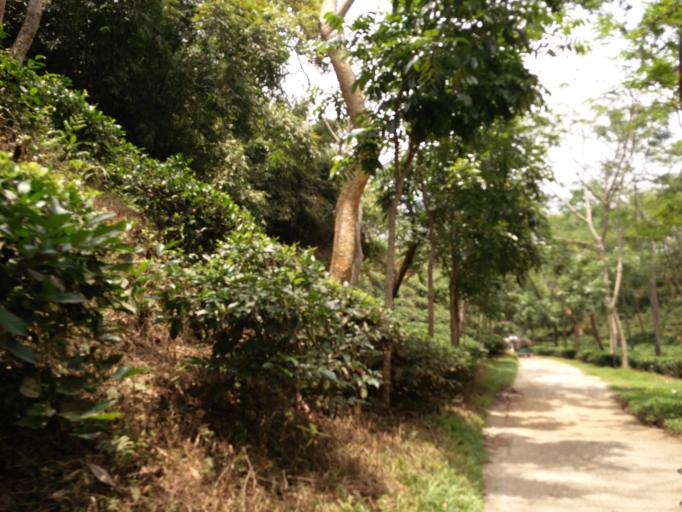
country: IN
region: Tripura
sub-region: Dhalai
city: Kamalpur
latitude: 24.3020
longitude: 91.8000
